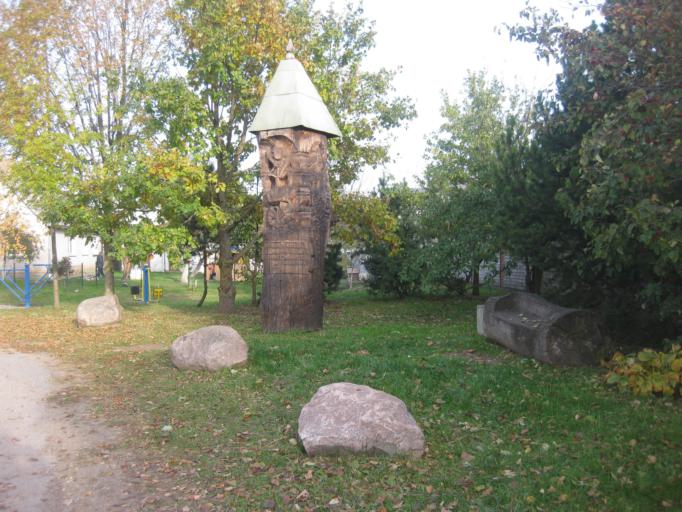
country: LT
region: Kauno apskritis
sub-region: Kaunas
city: Aleksotas
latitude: 54.8889
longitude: 23.8759
